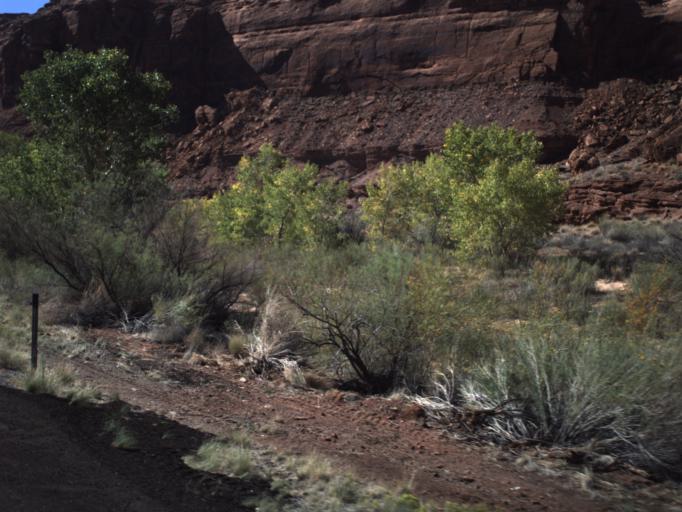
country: US
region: Utah
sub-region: San Juan County
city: Blanding
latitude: 37.9515
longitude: -110.4757
